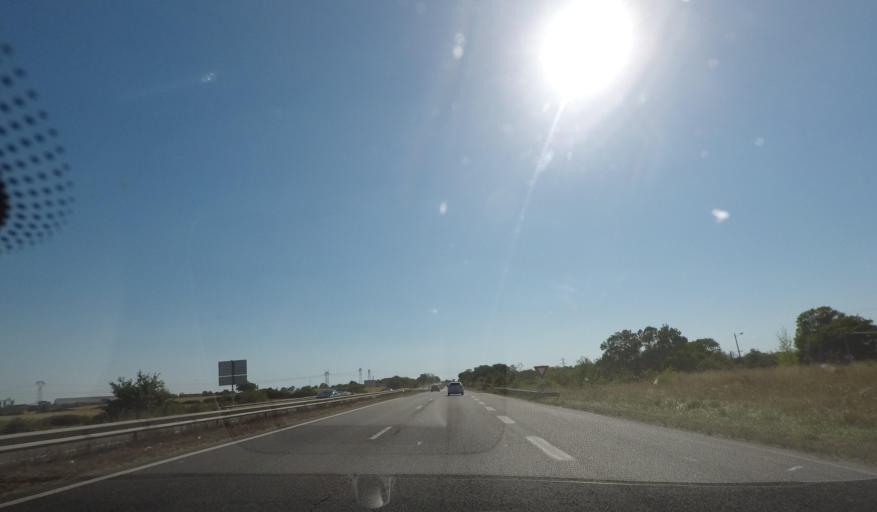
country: FR
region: Pays de la Loire
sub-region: Departement de la Loire-Atlantique
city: Montoir-de-Bretagne
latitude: 47.3374
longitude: -2.1121
